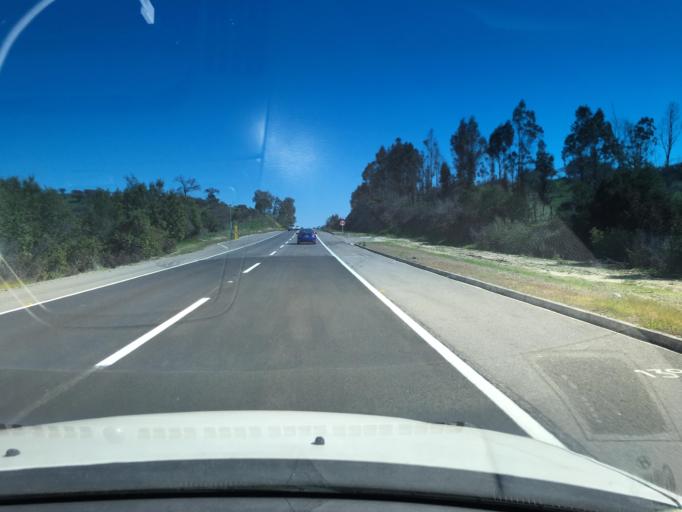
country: CL
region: Valparaiso
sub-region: San Antonio Province
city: El Tabo
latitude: -33.3953
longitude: -71.4889
